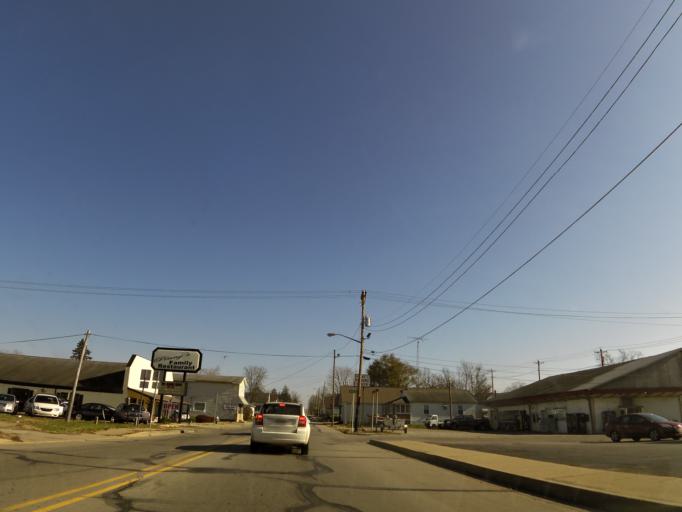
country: US
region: Indiana
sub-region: Fayette County
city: Connersville
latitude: 39.6389
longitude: -85.1284
